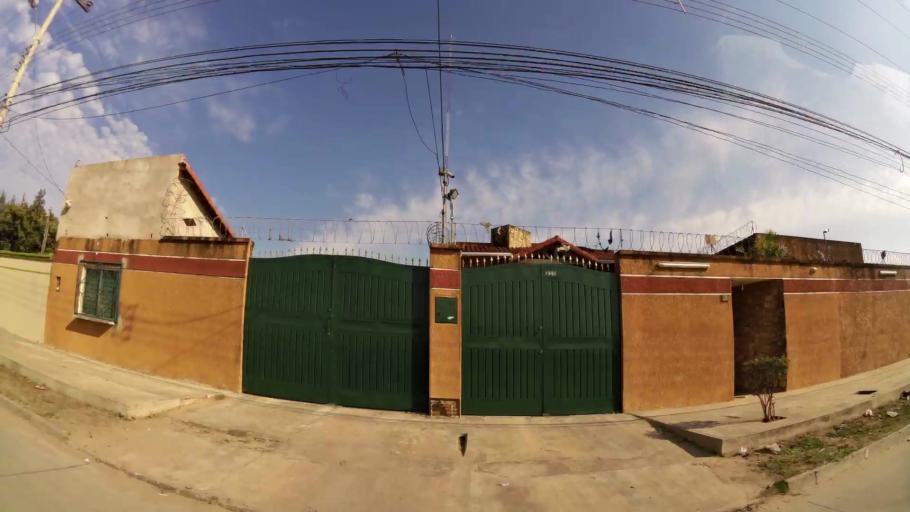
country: BO
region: Santa Cruz
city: Santa Cruz de la Sierra
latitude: -17.7437
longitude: -63.1475
